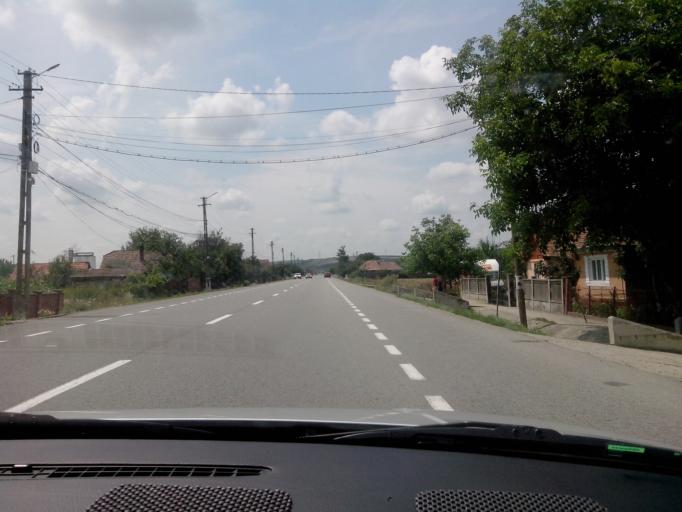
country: RO
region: Cluj
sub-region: Comuna Iclod
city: Iclod
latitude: 46.9464
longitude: 23.7935
